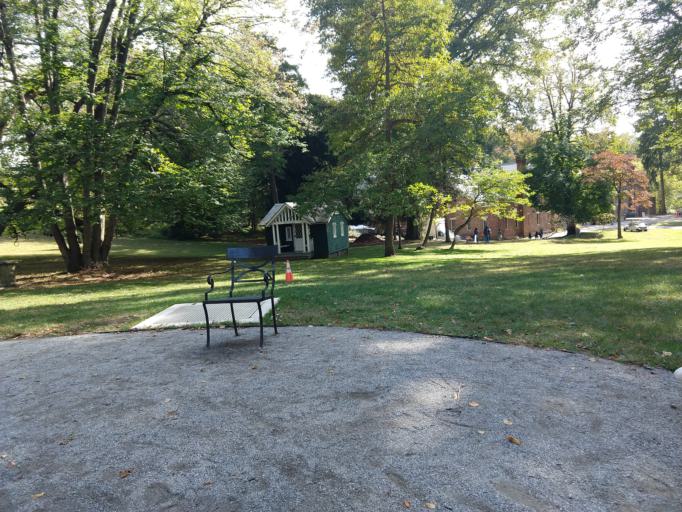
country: US
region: New York
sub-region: Westchester County
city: Irvington
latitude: 41.0537
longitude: -73.8669
